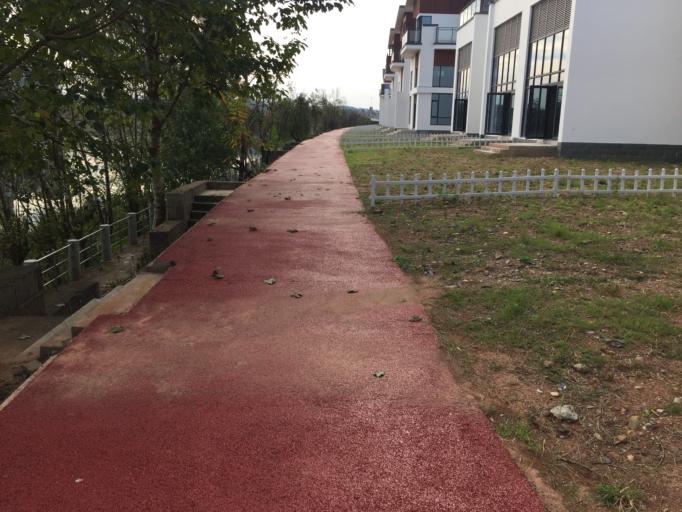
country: CN
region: Anhui Sheng
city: Xintan
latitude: 29.7243
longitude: 118.2863
